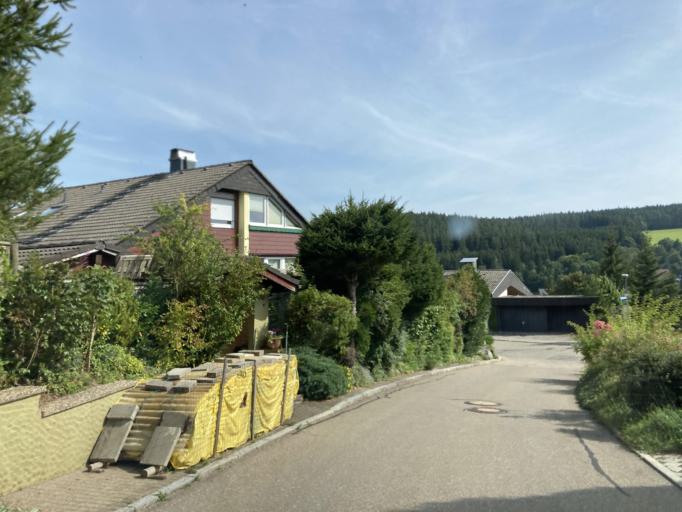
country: DE
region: Baden-Wuerttemberg
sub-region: Freiburg Region
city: Sankt Georgen im Schwarzwald
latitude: 48.1167
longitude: 8.3075
